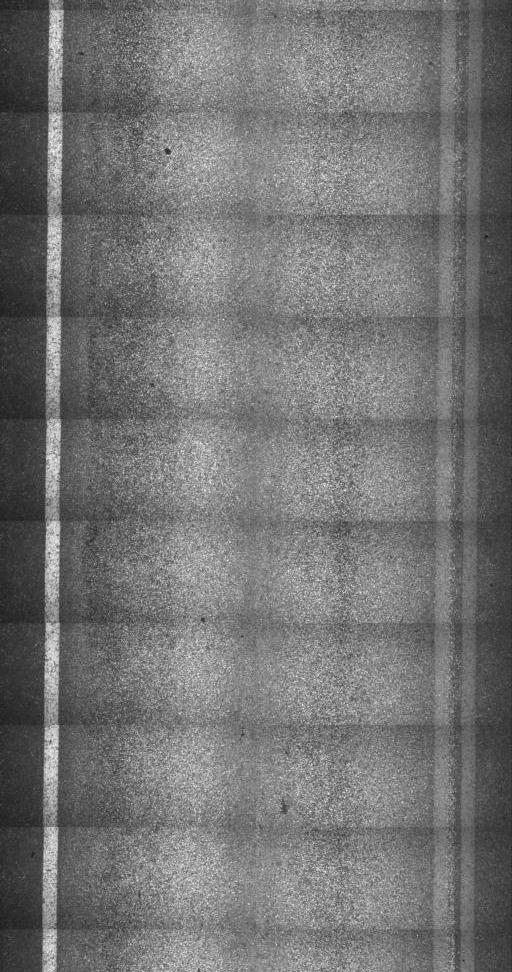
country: US
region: Vermont
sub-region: Grand Isle County
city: North Hero
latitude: 44.7184
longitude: -73.2955
